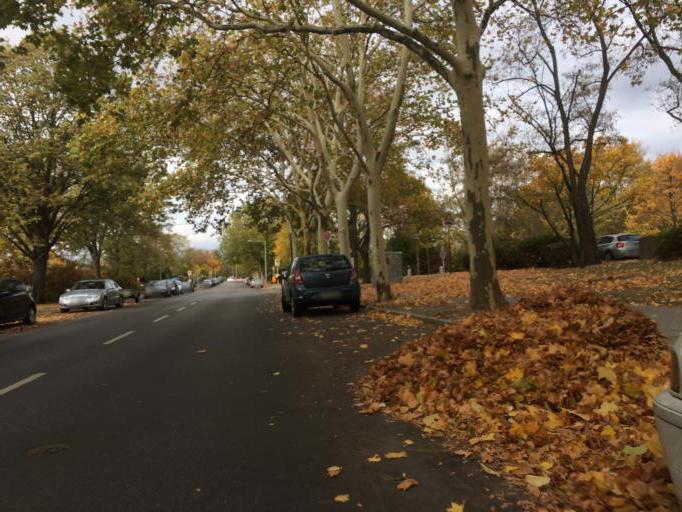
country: DE
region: Berlin
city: Lubars
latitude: 52.6060
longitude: 13.3491
